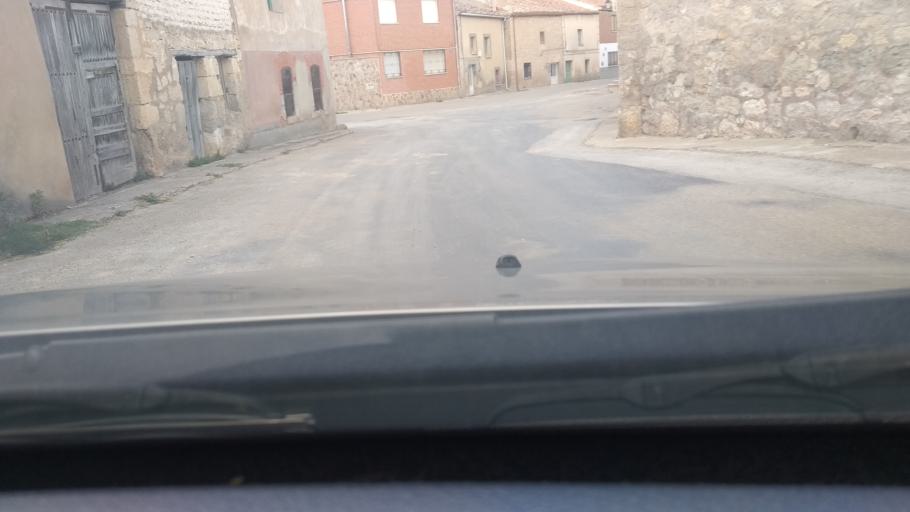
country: ES
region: Castille and Leon
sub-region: Provincia de Burgos
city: Villafruela
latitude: 41.9164
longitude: -3.9127
